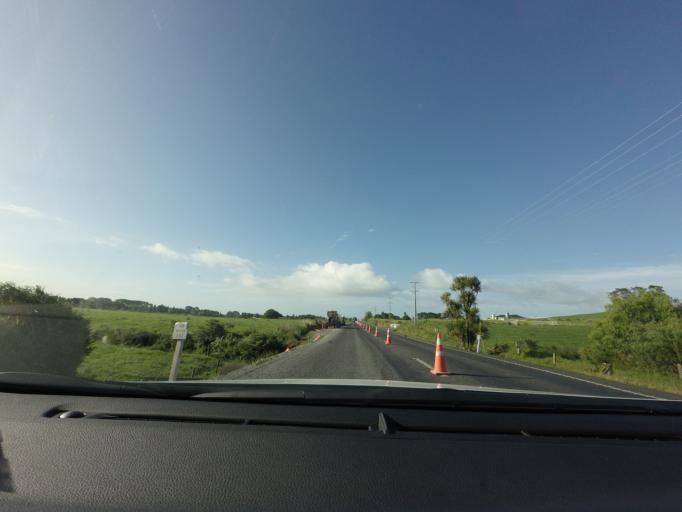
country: NZ
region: Waikato
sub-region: Hauraki District
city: Ngatea
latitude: -37.4660
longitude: 175.5101
